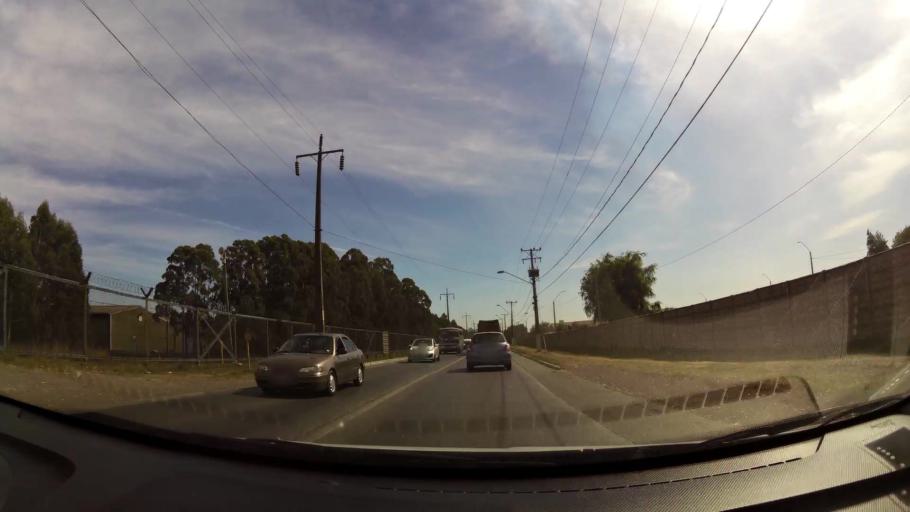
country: CL
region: Biobio
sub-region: Provincia de Concepcion
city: Talcahuano
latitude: -36.7379
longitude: -73.1208
